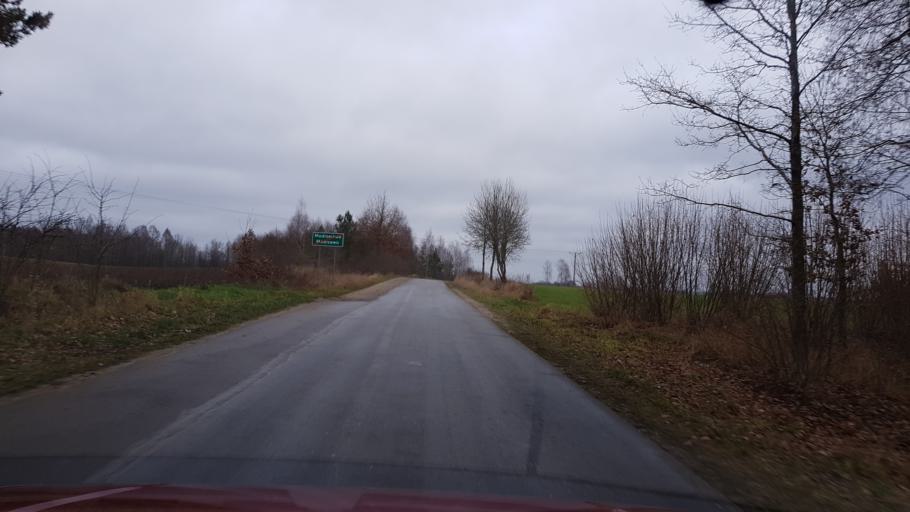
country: PL
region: Pomeranian Voivodeship
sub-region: Powiat bytowski
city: Tuchomie
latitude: 54.1554
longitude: 17.3296
